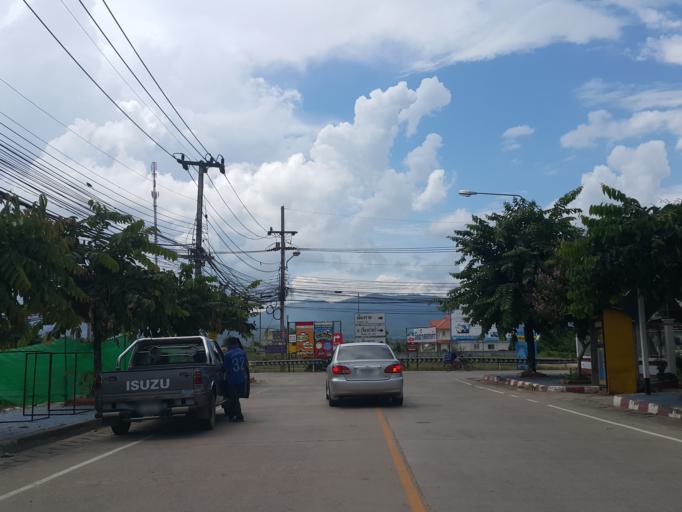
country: TH
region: Chiang Mai
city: Phrao
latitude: 19.3653
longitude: 99.2011
